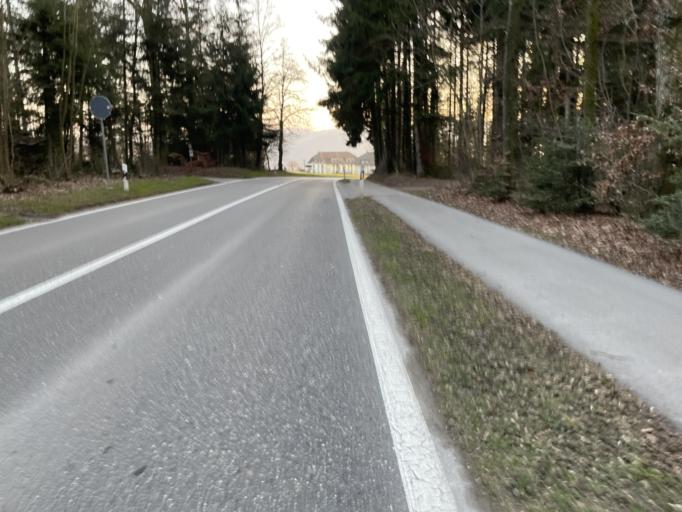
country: CH
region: Bern
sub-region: Bern-Mittelland District
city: Rubigen
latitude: 46.9027
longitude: 7.5538
